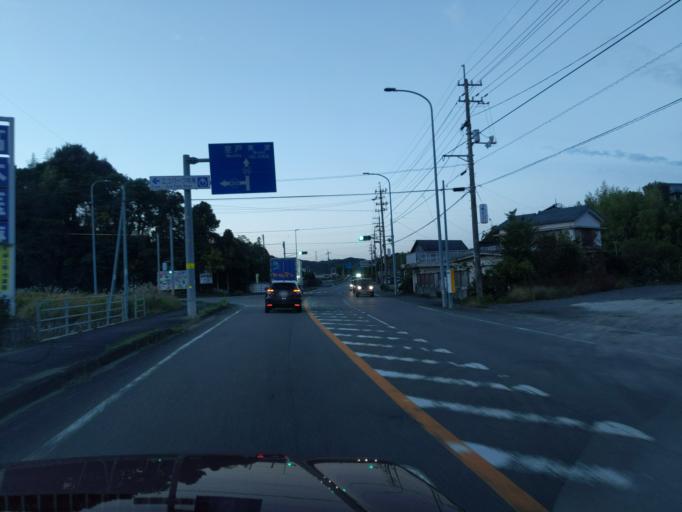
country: JP
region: Tokushima
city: Anan
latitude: 33.8468
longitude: 134.6260
